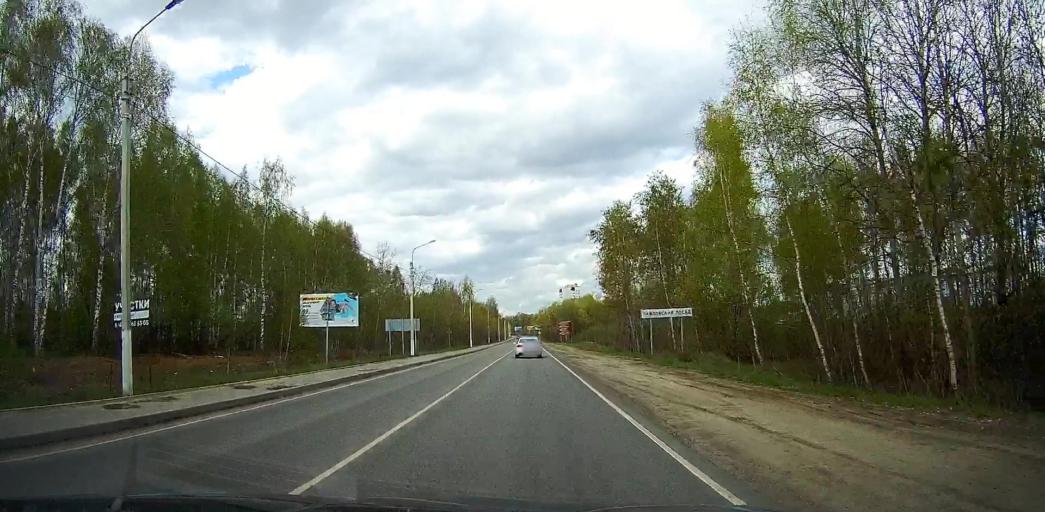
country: RU
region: Moskovskaya
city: Pavlovskiy Posad
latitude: 55.7595
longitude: 38.6562
